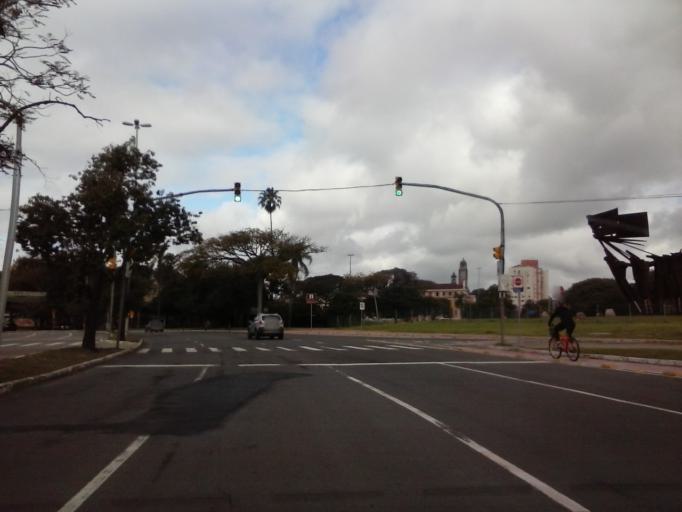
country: BR
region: Rio Grande do Sul
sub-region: Porto Alegre
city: Porto Alegre
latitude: -30.0383
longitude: -51.2298
